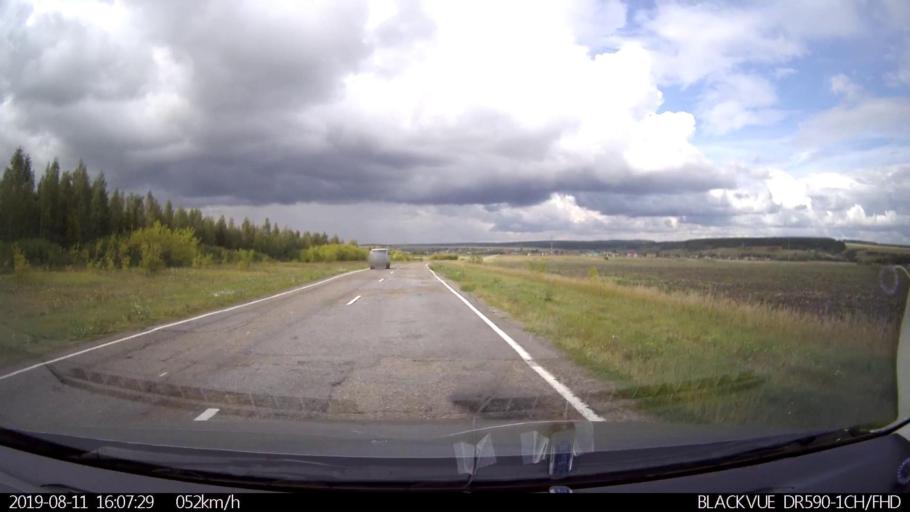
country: RU
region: Ulyanovsk
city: Ignatovka
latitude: 53.9776
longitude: 47.6465
